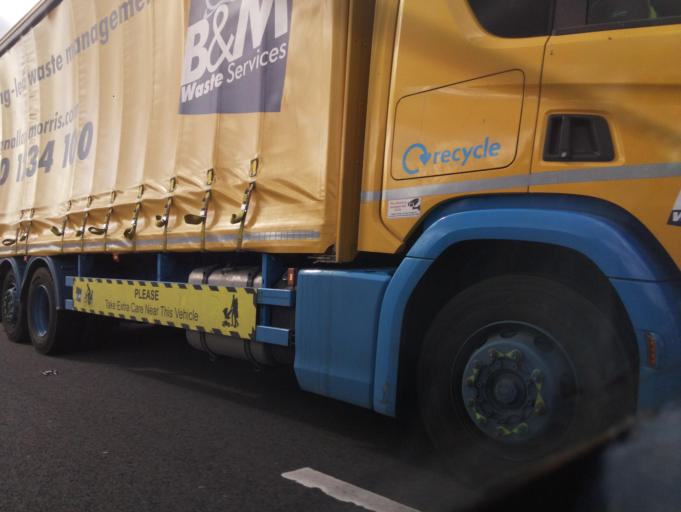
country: GB
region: England
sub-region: Borough of Wigan
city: Shevington
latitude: 53.5933
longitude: -2.6939
